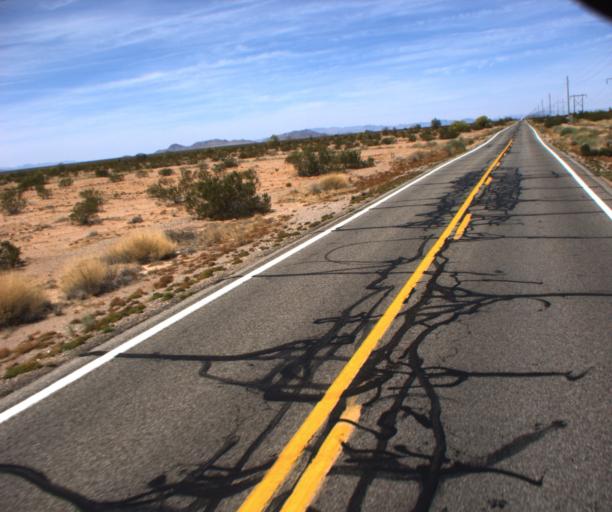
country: US
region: Arizona
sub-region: La Paz County
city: Quartzsite
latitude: 33.8332
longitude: -114.2170
